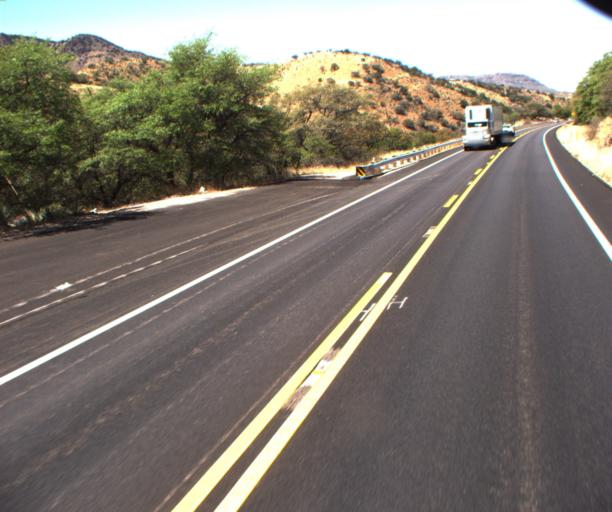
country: US
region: Arizona
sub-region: Cochise County
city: Bisbee
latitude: 31.4756
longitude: -109.9756
